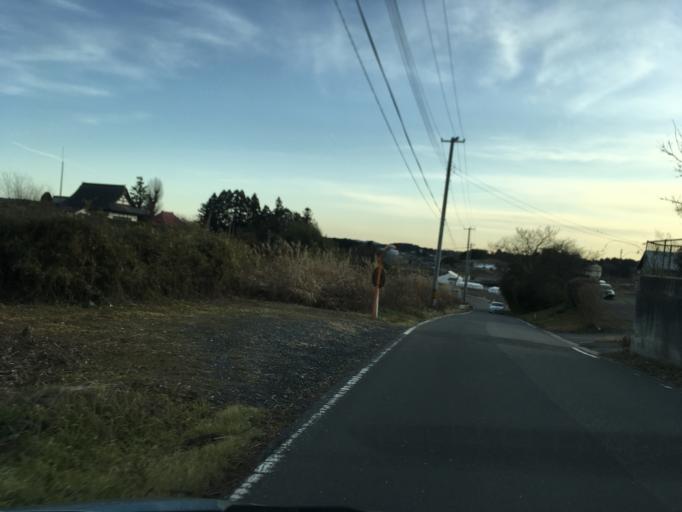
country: JP
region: Miyagi
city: Kogota
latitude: 38.6916
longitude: 141.0955
